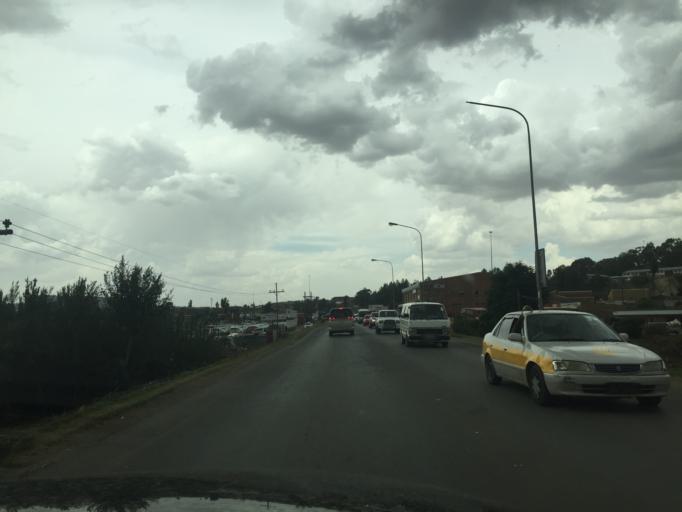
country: LS
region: Maseru
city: Maseru
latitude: -29.3031
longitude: 27.5162
